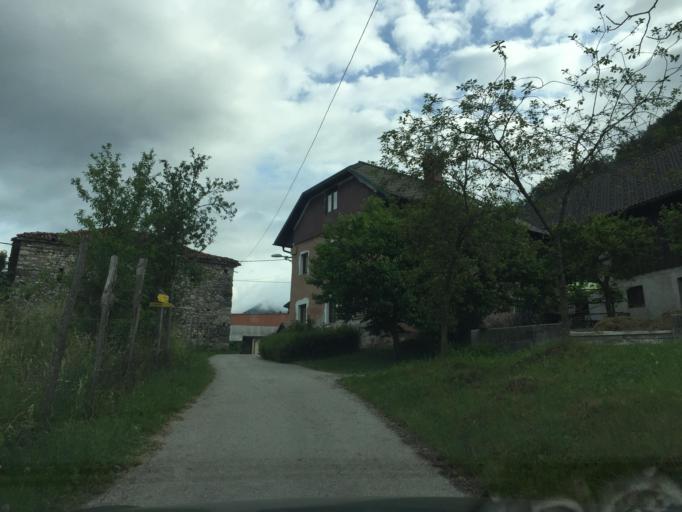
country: SI
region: Tolmin
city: Tolmin
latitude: 46.1674
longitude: 13.8374
